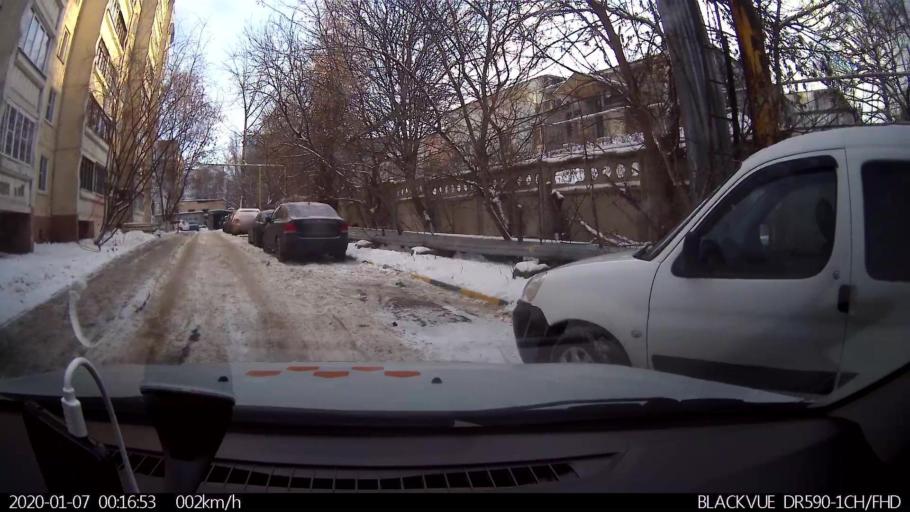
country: RU
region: Nizjnij Novgorod
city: Nizhniy Novgorod
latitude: 56.2347
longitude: 43.9446
